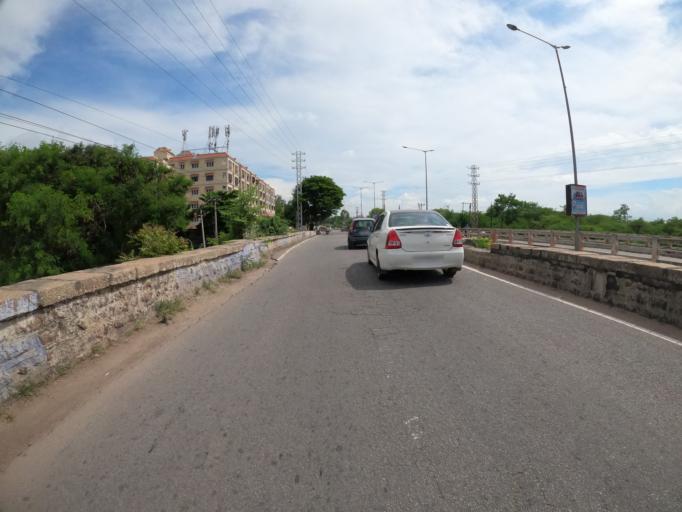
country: IN
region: Telangana
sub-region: Hyderabad
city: Hyderabad
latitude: 17.3718
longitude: 78.4050
